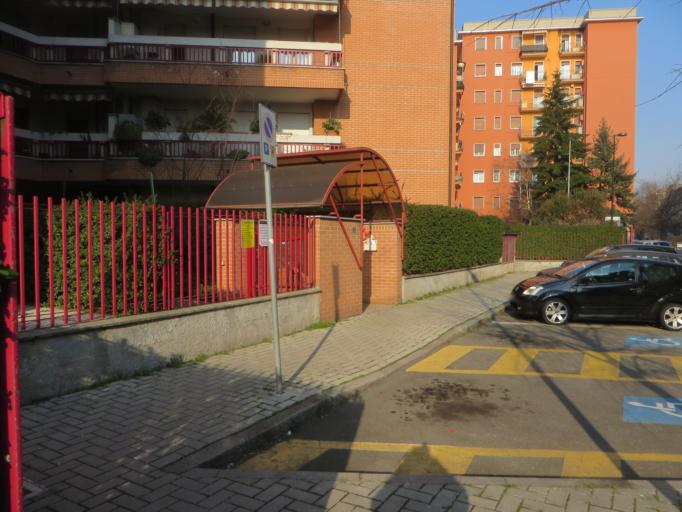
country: IT
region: Lombardy
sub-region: Citta metropolitana di Milano
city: Cormano
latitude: 45.5459
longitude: 9.1606
